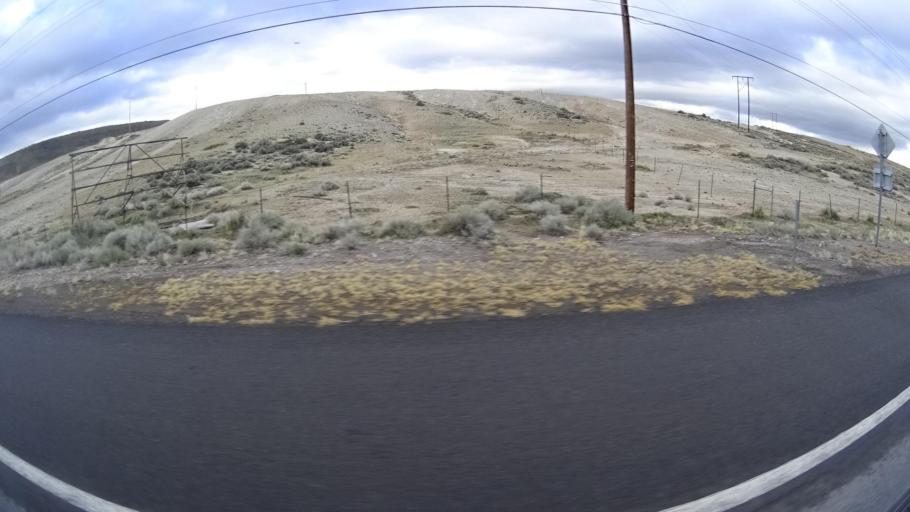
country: US
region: Nevada
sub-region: Storey County
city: Virginia City
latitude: 39.3894
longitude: -119.7414
